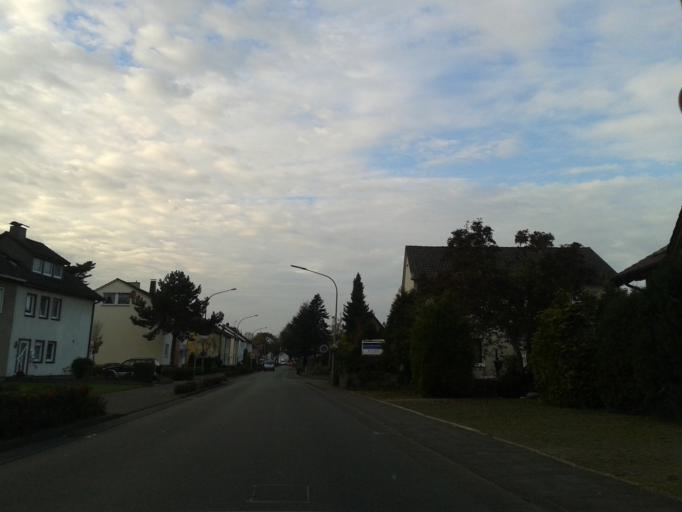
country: DE
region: North Rhine-Westphalia
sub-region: Regierungsbezirk Detmold
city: Paderborn
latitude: 51.7628
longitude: 8.7269
